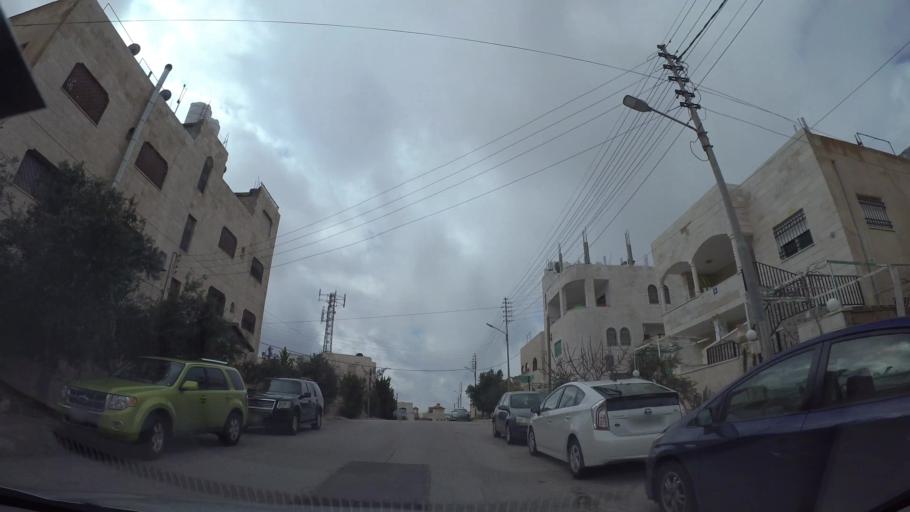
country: JO
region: Amman
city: Al Jubayhah
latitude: 32.0651
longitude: 35.8789
